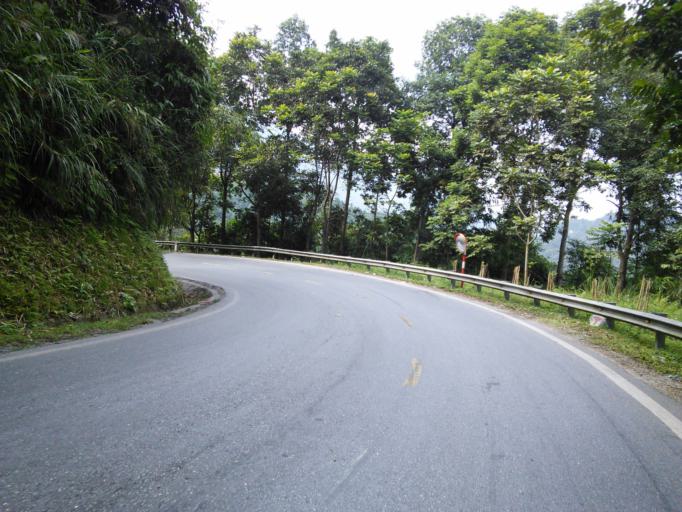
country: VN
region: Lao Cai
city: Lao Cai
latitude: 22.4466
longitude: 103.9371
